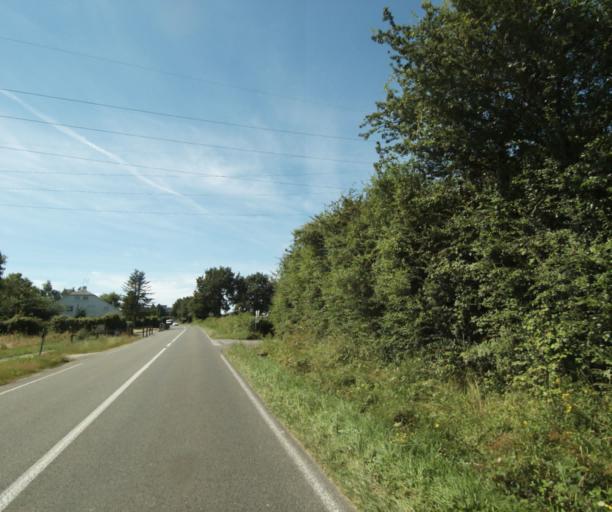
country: FR
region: Pays de la Loire
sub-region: Departement de la Mayenne
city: Laval
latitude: 48.0511
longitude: -0.7904
